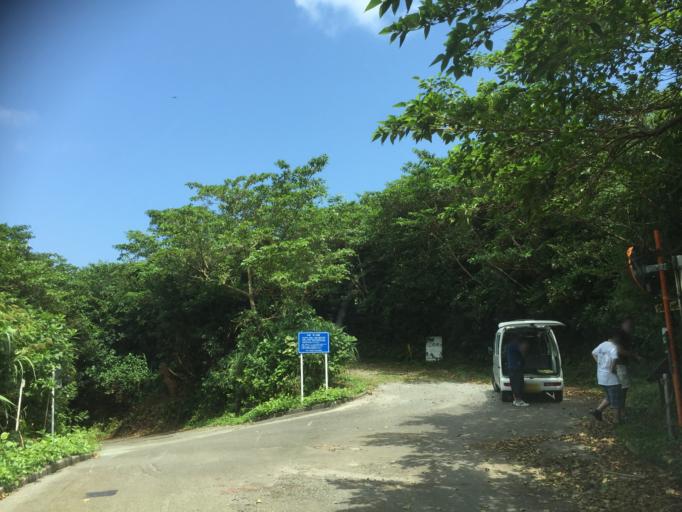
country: JP
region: Shizuoka
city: Shimoda
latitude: 34.0914
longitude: 139.5019
